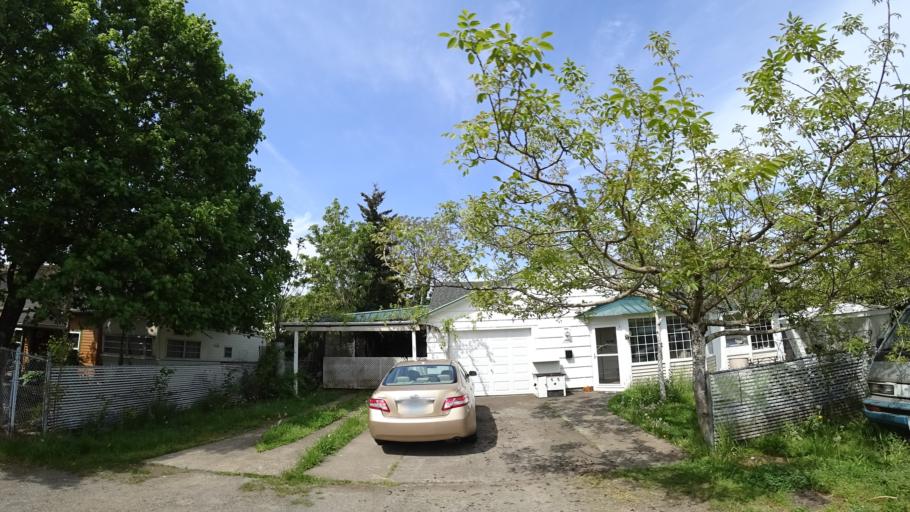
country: US
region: Oregon
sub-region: Clackamas County
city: Milwaukie
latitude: 45.4719
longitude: -122.6087
